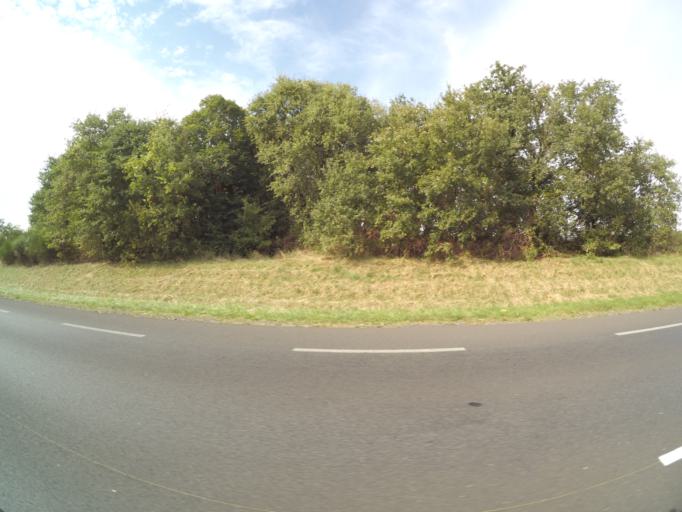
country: FR
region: Pays de la Loire
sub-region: Departement de Maine-et-Loire
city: Distre
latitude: 47.2409
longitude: -0.1110
